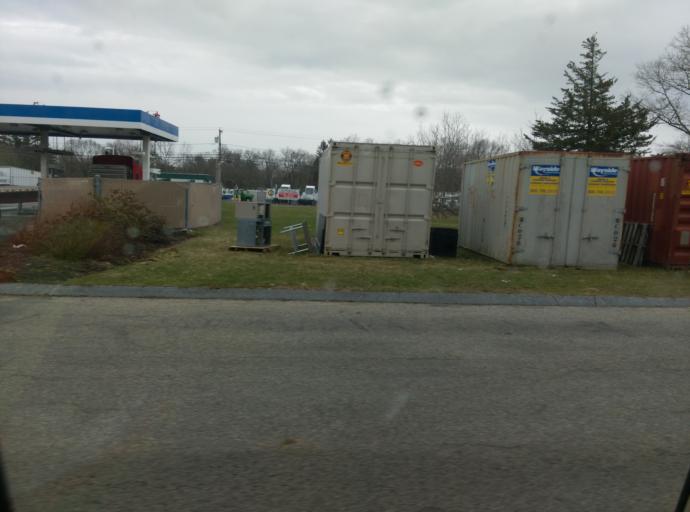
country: US
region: New Hampshire
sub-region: Rockingham County
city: Seabrook
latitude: 42.8696
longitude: -70.8850
